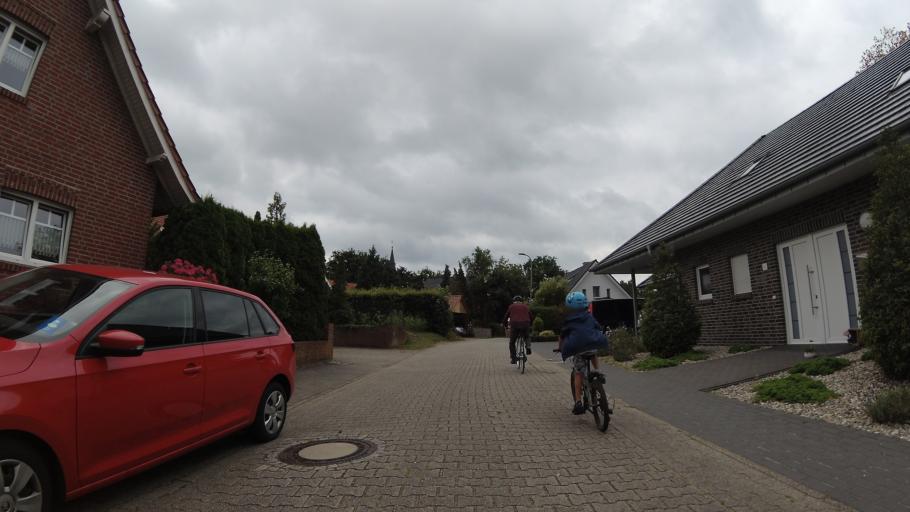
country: DE
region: Lower Saxony
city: Lathen
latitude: 52.8638
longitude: 7.3117
